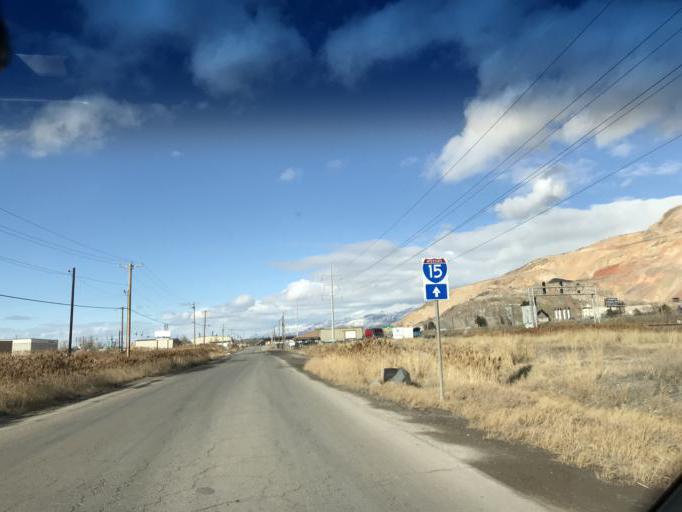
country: US
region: Utah
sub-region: Davis County
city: North Salt Lake
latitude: 40.8075
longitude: -111.9208
